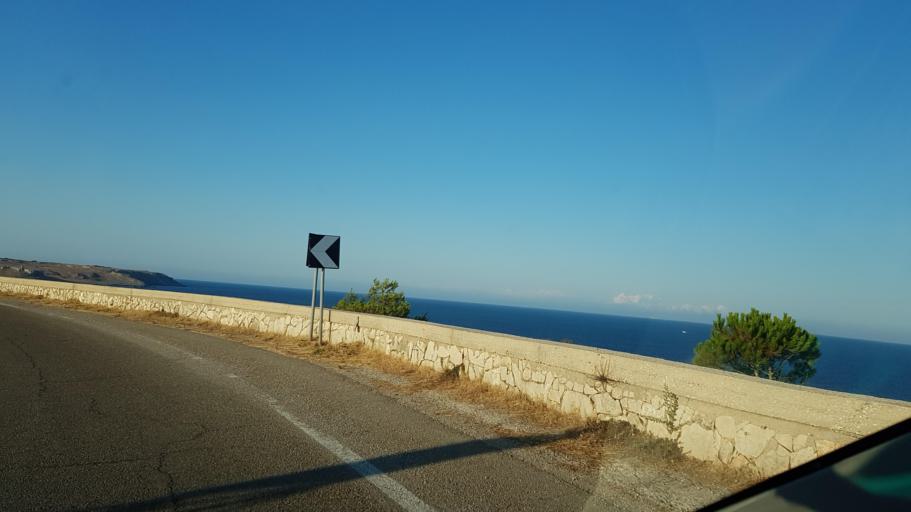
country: IT
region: Apulia
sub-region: Provincia di Lecce
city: Cerfignano
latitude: 40.0665
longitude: 18.4797
